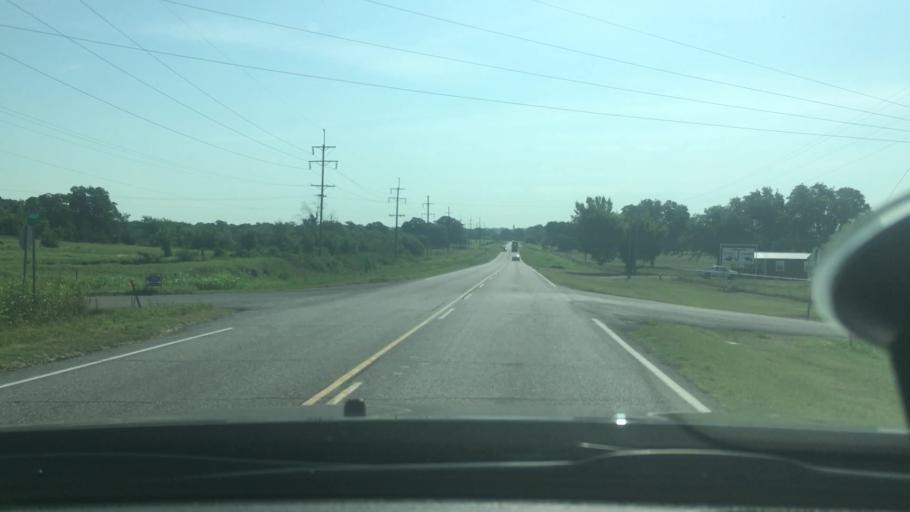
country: US
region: Oklahoma
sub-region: Garvin County
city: Wynnewood
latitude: 34.6516
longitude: -97.2131
